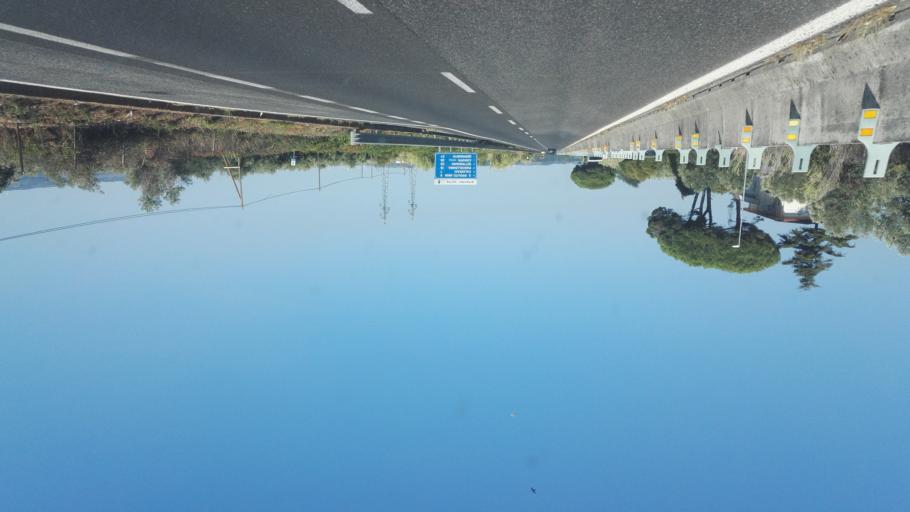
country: IT
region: Calabria
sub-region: Provincia di Catanzaro
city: Santa Eufemia Lamezia
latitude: 38.9136
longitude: 16.2926
